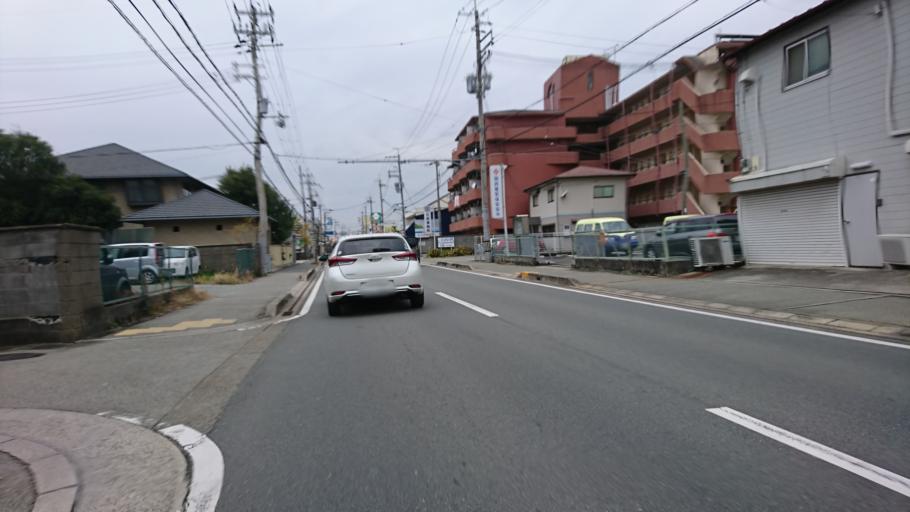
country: JP
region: Hyogo
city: Kakogawacho-honmachi
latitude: 34.7614
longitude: 134.8327
